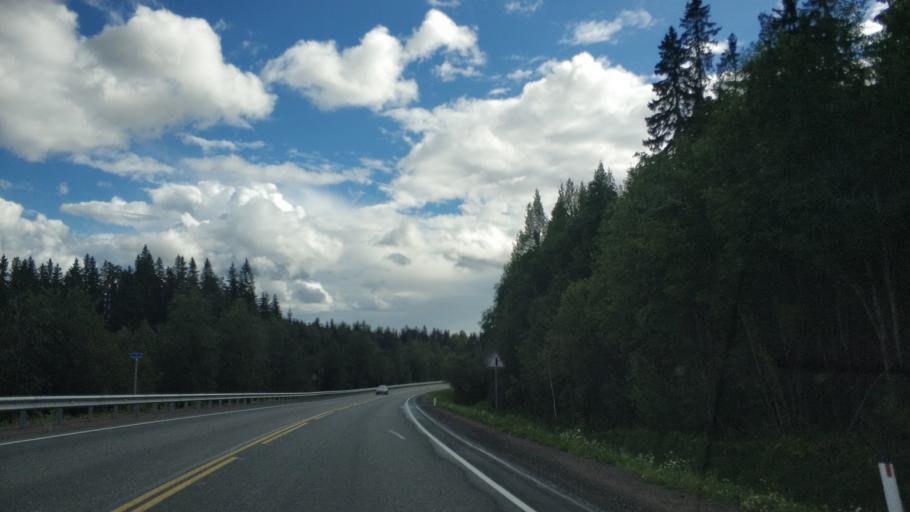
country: RU
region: Republic of Karelia
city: Khelyulya
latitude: 61.7843
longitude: 30.6539
